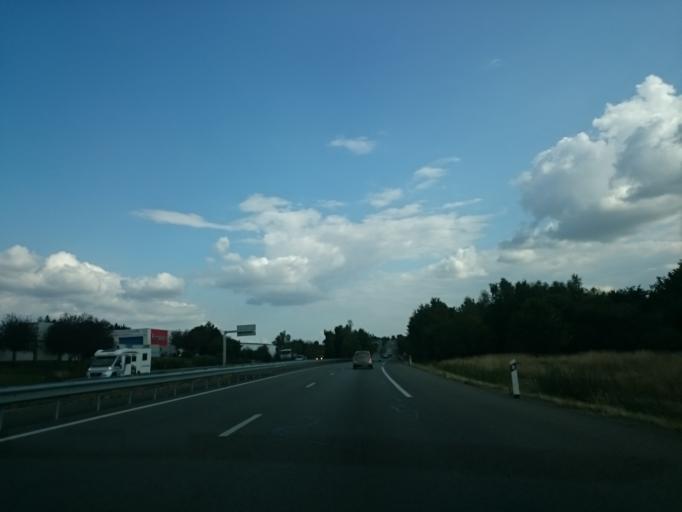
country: FR
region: Brittany
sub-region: Departement d'Ille-et-Vilaine
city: Crevin
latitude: 47.9607
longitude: -1.6864
